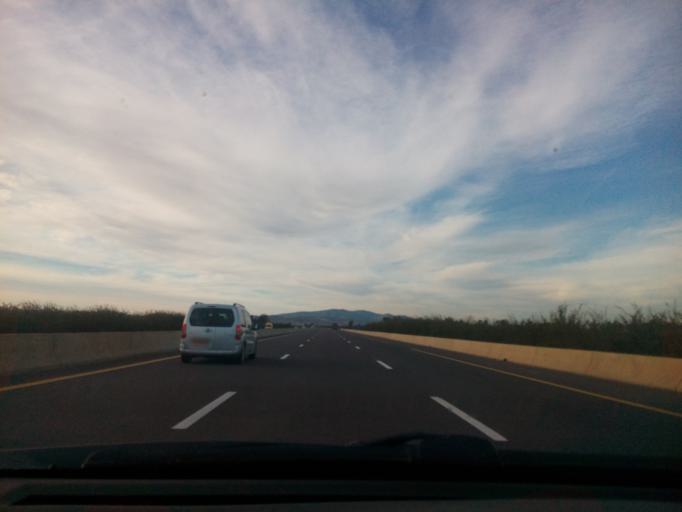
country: DZ
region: Mascara
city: Mascara
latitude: 35.6323
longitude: 0.0856
